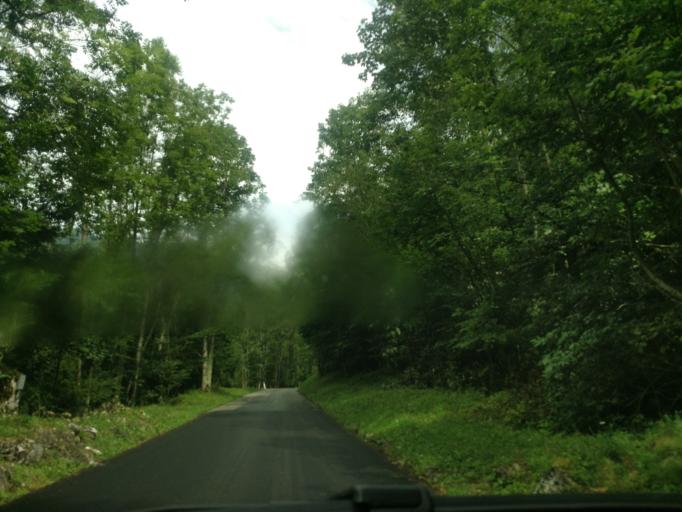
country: IT
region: Veneto
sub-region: Provincia di Belluno
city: Don
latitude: 46.2161
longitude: 11.9933
